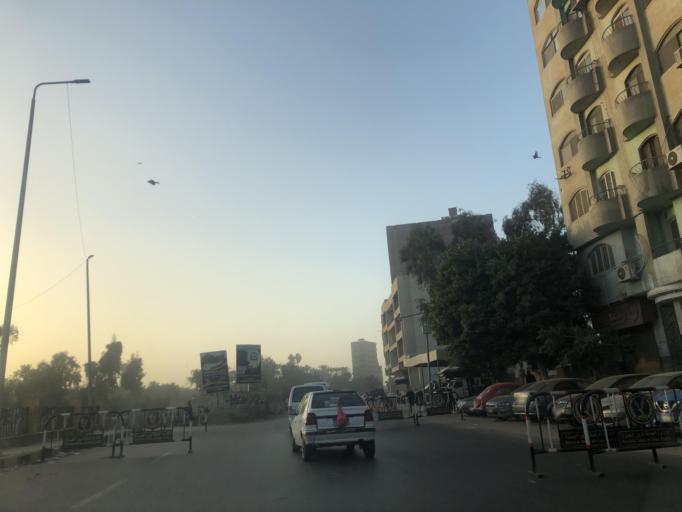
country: EG
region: Al Jizah
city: Al Jizah
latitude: 29.9711
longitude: 31.1773
